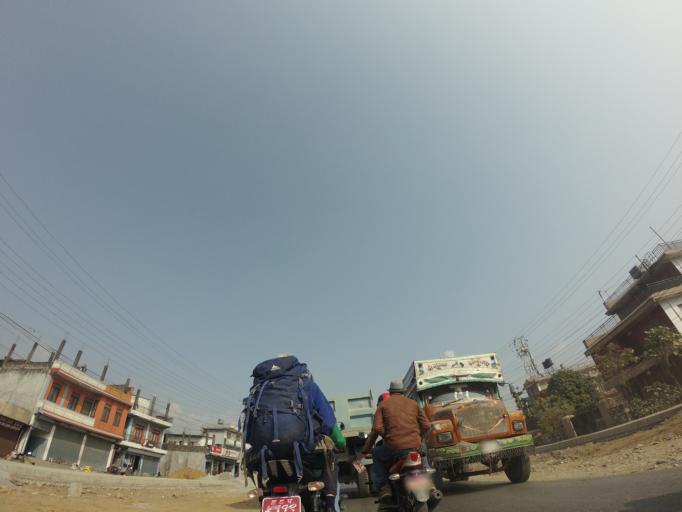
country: NP
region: Western Region
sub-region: Gandaki Zone
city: Pokhara
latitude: 28.2195
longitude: 83.9775
